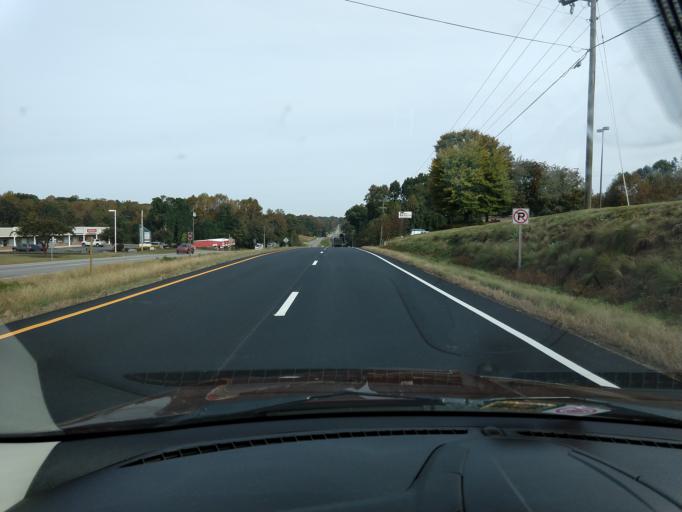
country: US
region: Virginia
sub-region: Pittsylvania County
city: Chatham
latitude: 36.7920
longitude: -79.3937
